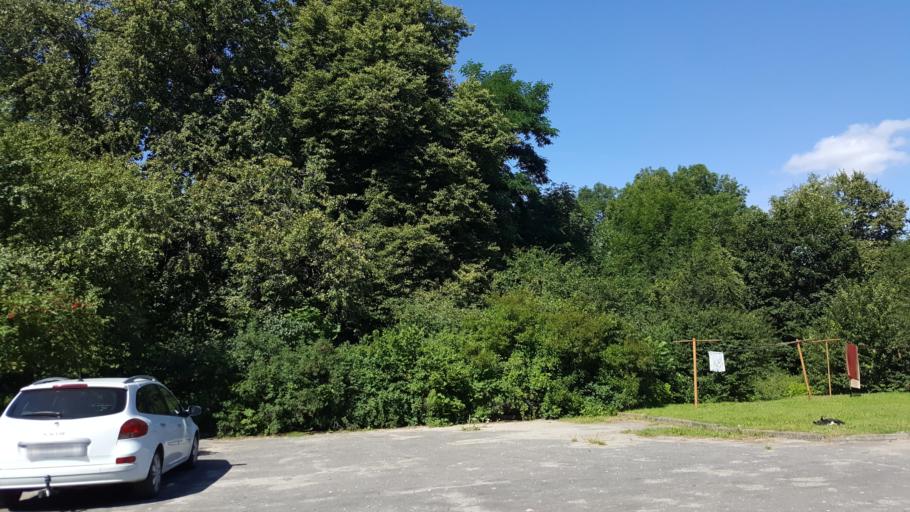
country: BY
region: Brest
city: Kamyanyets
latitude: 52.3851
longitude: 23.6556
